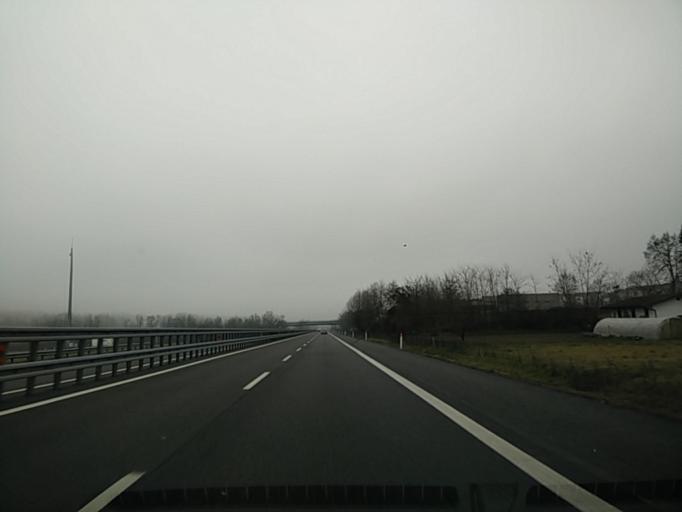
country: IT
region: Piedmont
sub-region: Provincia di Asti
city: Villafranca d'Asti
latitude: 44.9181
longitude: 8.0304
